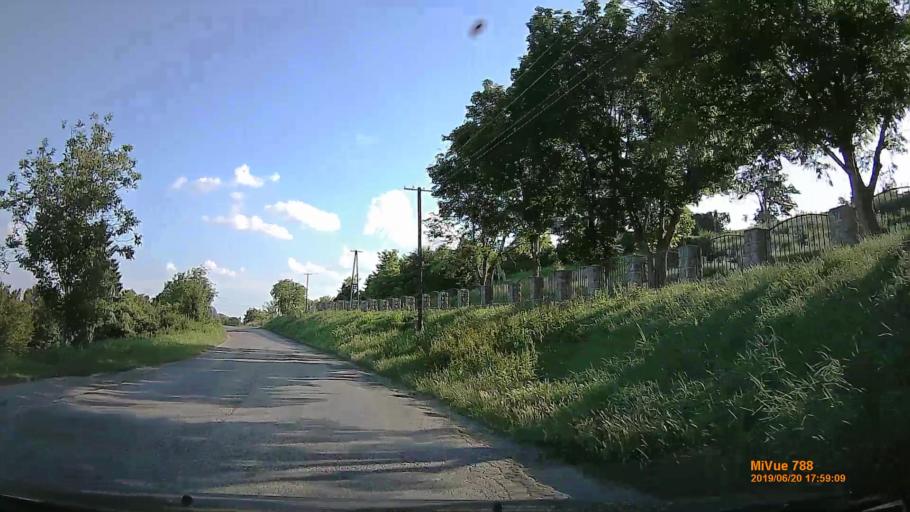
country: HU
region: Baranya
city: Buekkoesd
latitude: 46.0996
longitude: 17.9869
